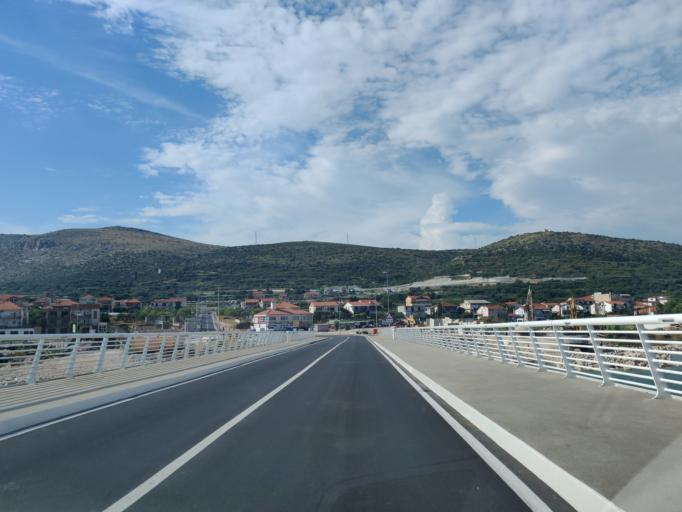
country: HR
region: Splitsko-Dalmatinska
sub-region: Grad Trogir
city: Trogir
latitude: 43.5206
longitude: 16.2649
